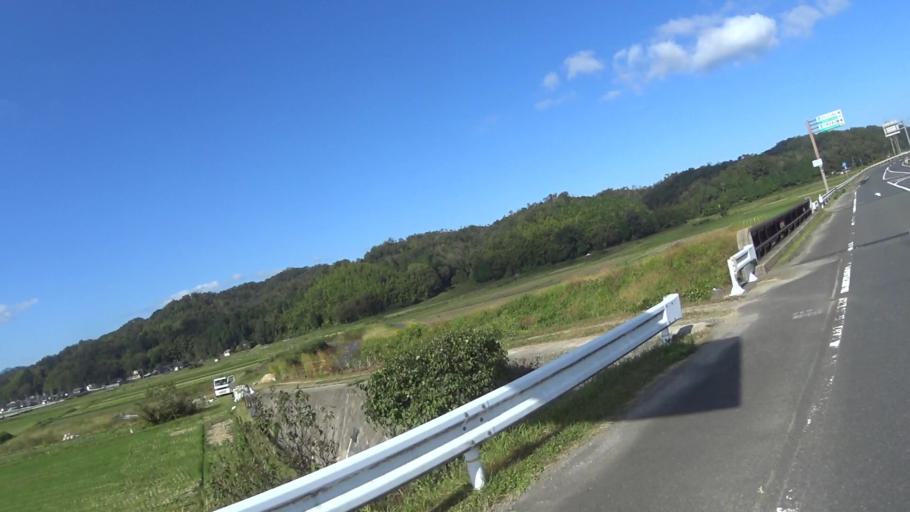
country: JP
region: Kyoto
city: Miyazu
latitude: 35.5977
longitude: 135.1401
